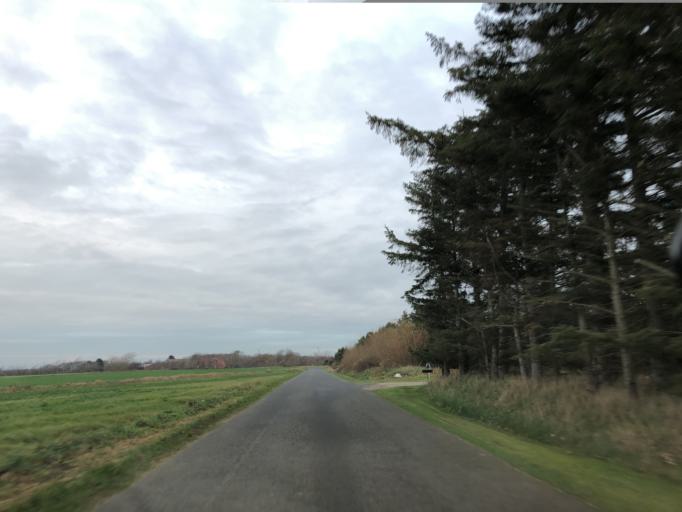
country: DK
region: Central Jutland
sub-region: Holstebro Kommune
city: Ulfborg
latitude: 56.2726
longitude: 8.2632
